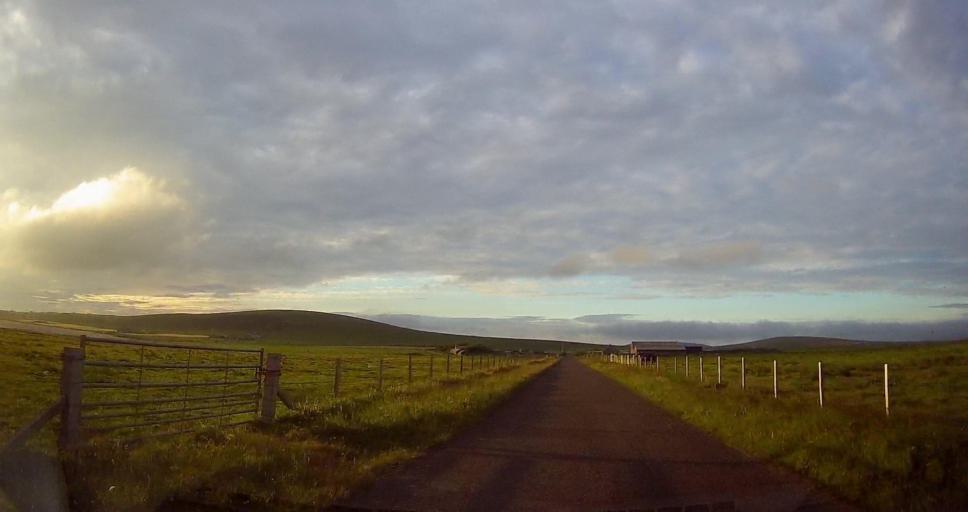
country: GB
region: Scotland
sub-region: Orkney Islands
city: Stromness
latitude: 59.1059
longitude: -3.2559
